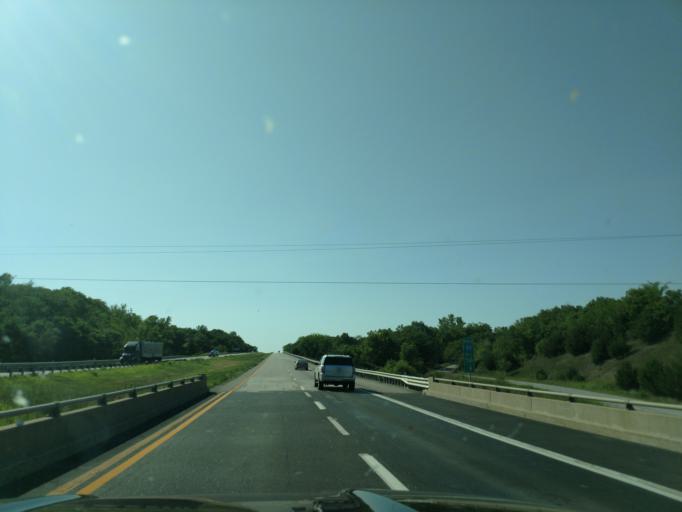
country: US
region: Missouri
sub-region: Andrew County
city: Savannah
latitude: 39.9037
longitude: -94.8846
